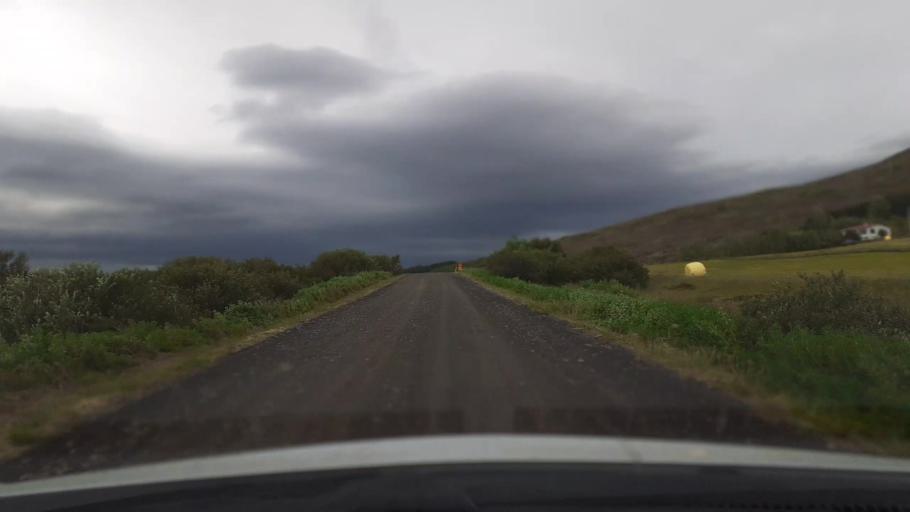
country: IS
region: Capital Region
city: Mosfellsbaer
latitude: 64.5260
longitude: -21.4826
